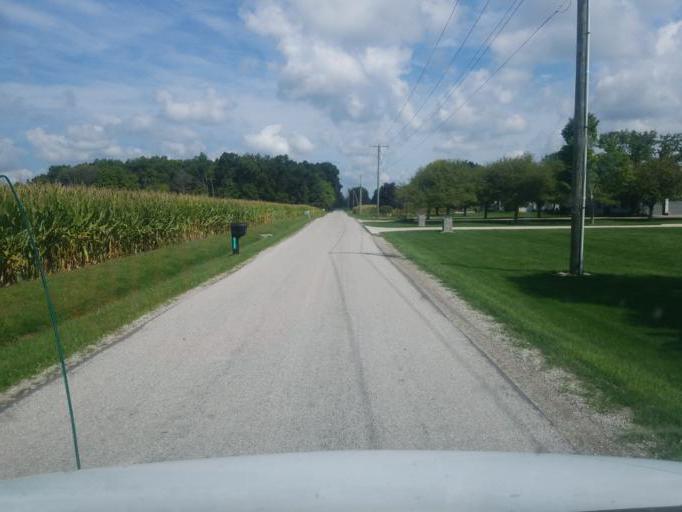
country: US
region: Ohio
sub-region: Marion County
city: Marion
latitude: 40.5149
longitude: -83.0838
